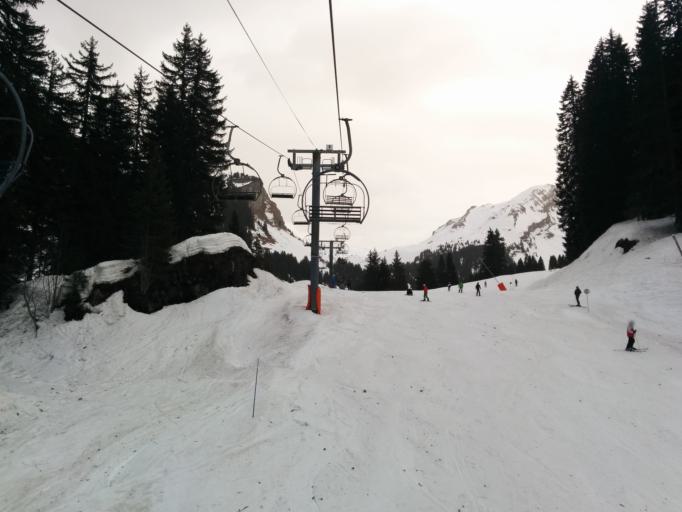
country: FR
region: Rhone-Alpes
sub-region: Departement de la Haute-Savoie
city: Morzine
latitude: 46.2051
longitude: 6.7805
